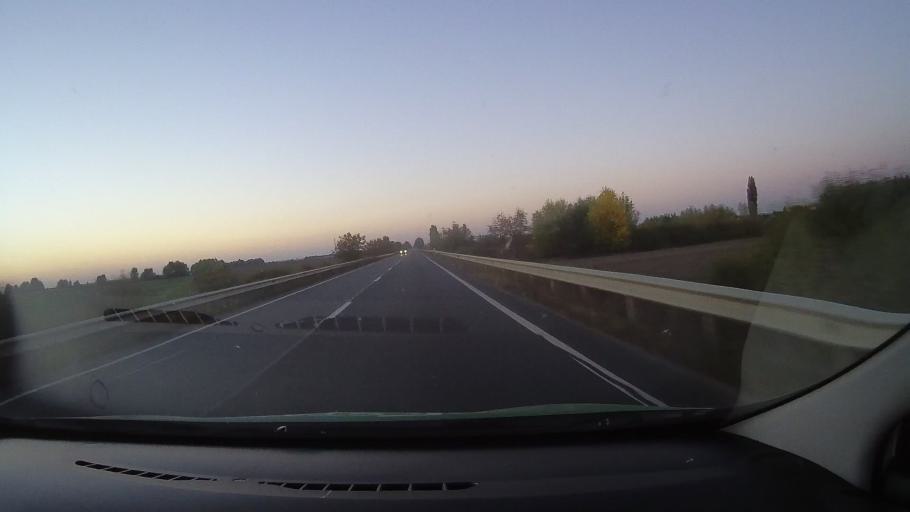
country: RO
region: Bihor
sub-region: Comuna Valea lui Mihai
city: Valea lui Mihai
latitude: 47.4889
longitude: 22.1566
